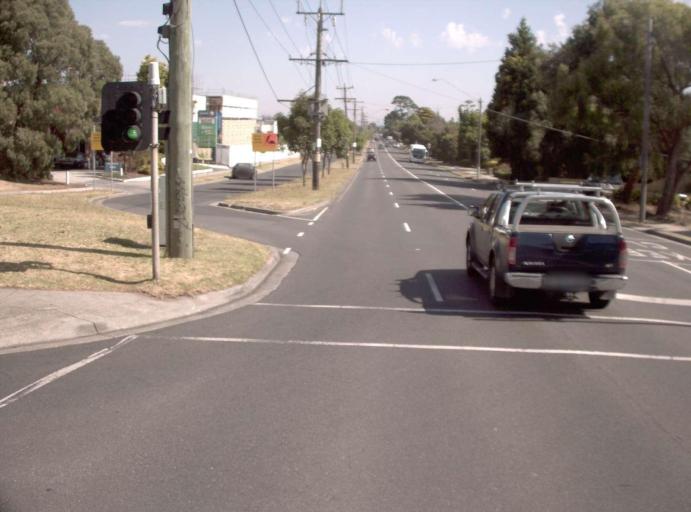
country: AU
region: Victoria
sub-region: Monash
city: Mulgrave
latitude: -37.9105
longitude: 145.1884
